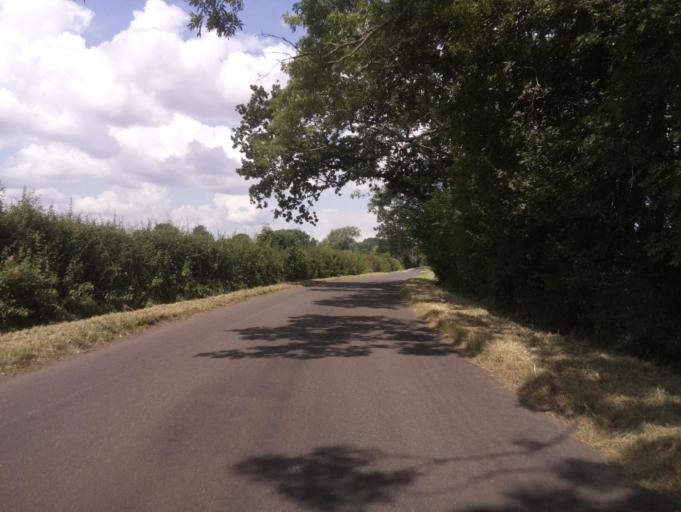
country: GB
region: England
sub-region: Wiltshire
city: Hankerton
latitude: 51.6227
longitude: -2.0215
